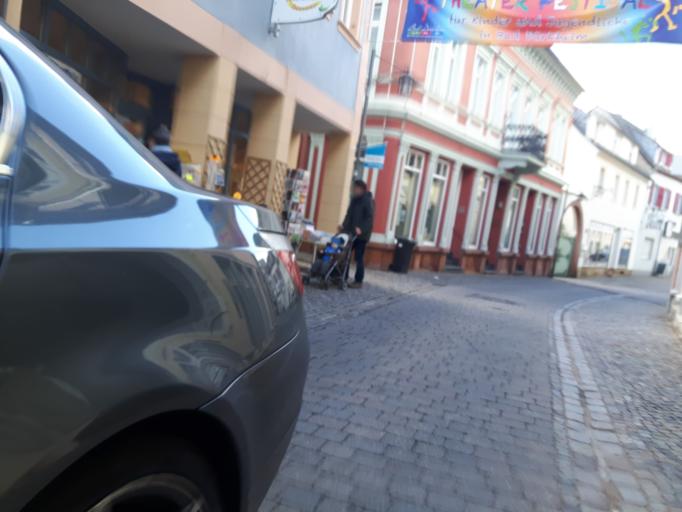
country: DE
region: Rheinland-Pfalz
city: Bad Duerkheim
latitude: 49.4603
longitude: 8.1663
